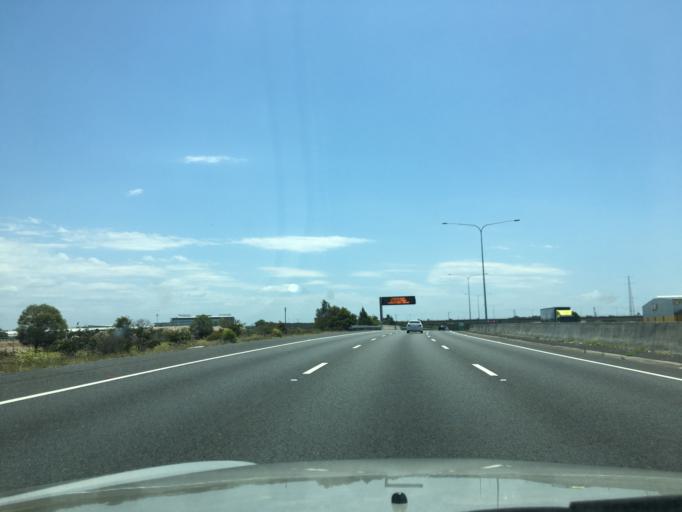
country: AU
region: Queensland
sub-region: Brisbane
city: Ascot
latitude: -27.4193
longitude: 153.0879
